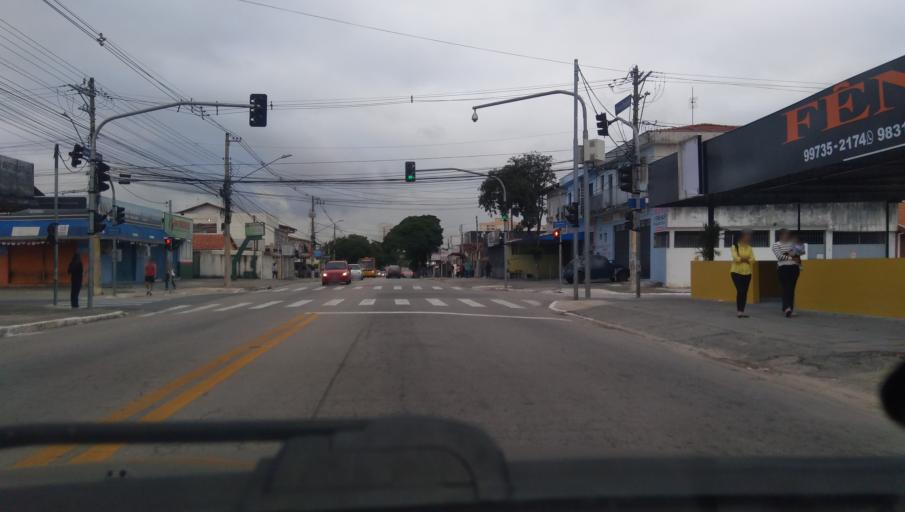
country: BR
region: Sao Paulo
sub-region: Sao Jose Dos Campos
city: Sao Jose dos Campos
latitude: -23.1749
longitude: -45.8541
